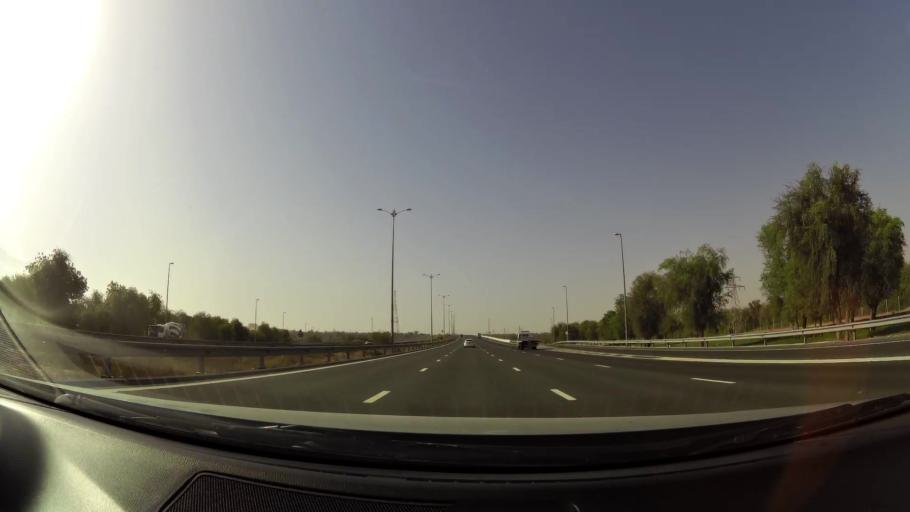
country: OM
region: Al Buraimi
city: Al Buraymi
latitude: 24.5877
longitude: 55.7394
